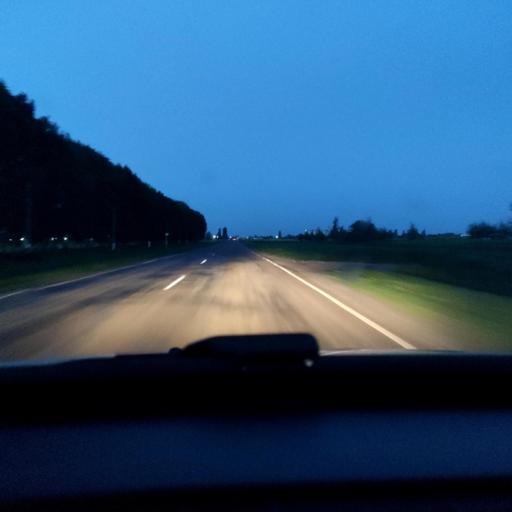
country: RU
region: Voronezj
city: Panino
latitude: 51.6509
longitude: 40.0972
